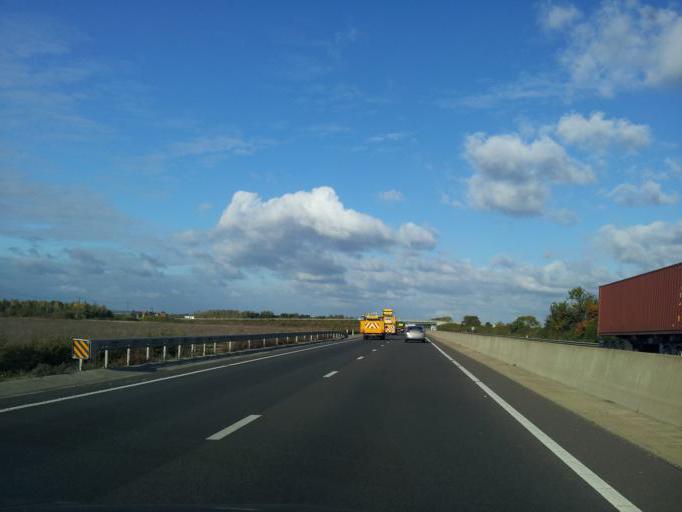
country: GB
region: England
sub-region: Bedford
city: Wootton
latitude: 52.0884
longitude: -0.5191
